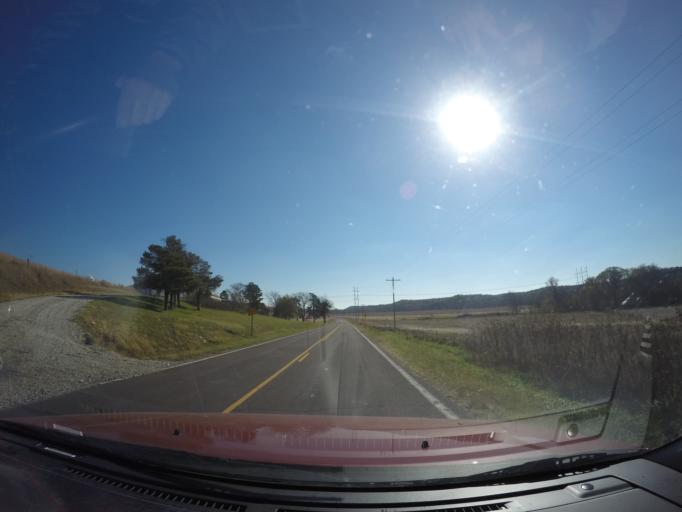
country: US
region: Kansas
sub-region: Geary County
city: Grandview Plaza
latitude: 38.9860
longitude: -96.7239
